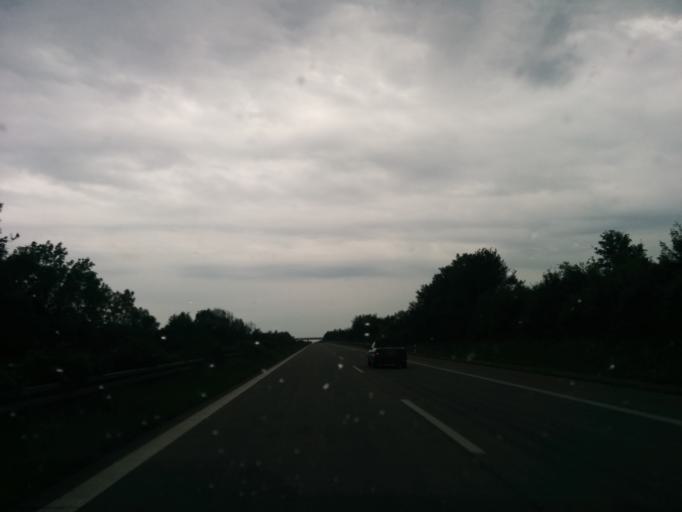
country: DE
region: Bavaria
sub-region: Regierungsbezirk Mittelfranken
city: Ohrenbach
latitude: 49.4684
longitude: 10.2326
